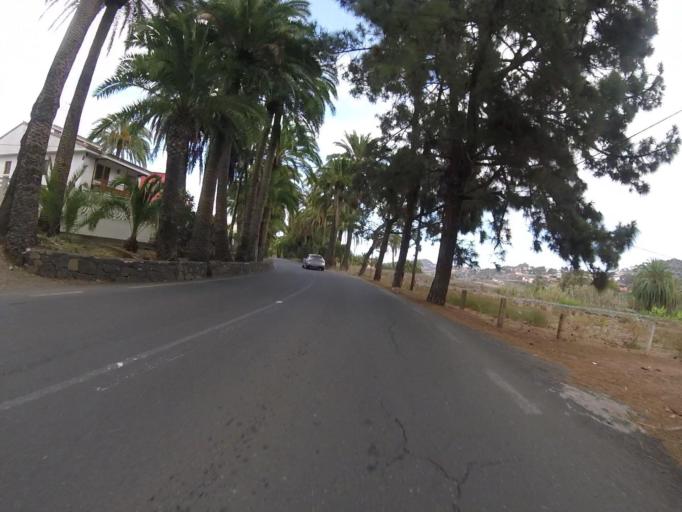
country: ES
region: Canary Islands
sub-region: Provincia de Las Palmas
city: Santa Brigida
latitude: 28.0356
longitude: -15.4959
